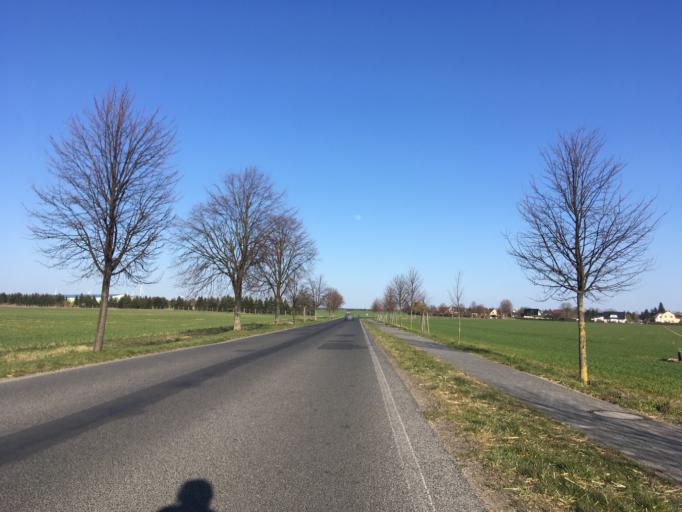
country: DE
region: Berlin
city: Falkenberg
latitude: 52.6034
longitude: 13.5392
